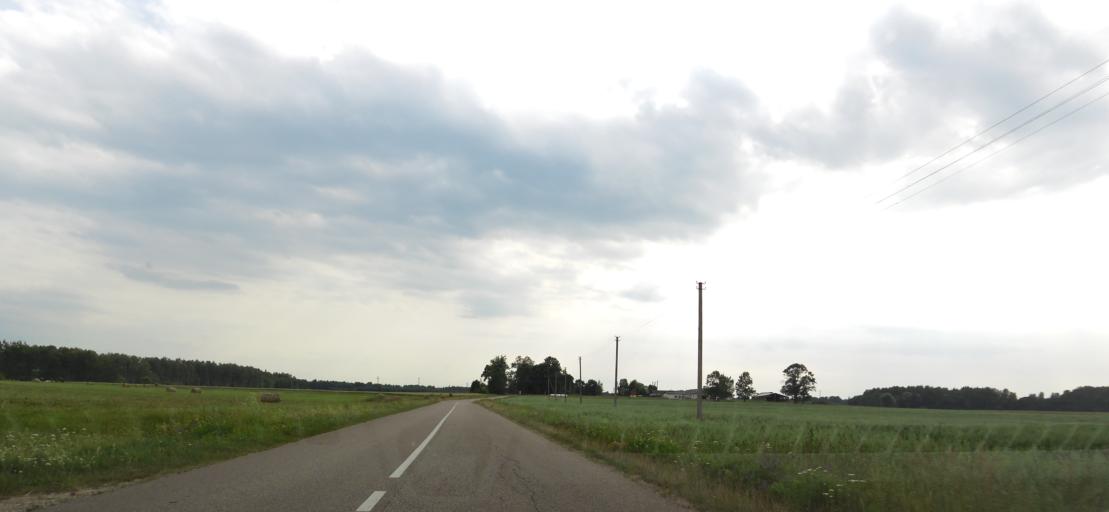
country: LT
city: Obeliai
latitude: 56.1395
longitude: 25.1283
